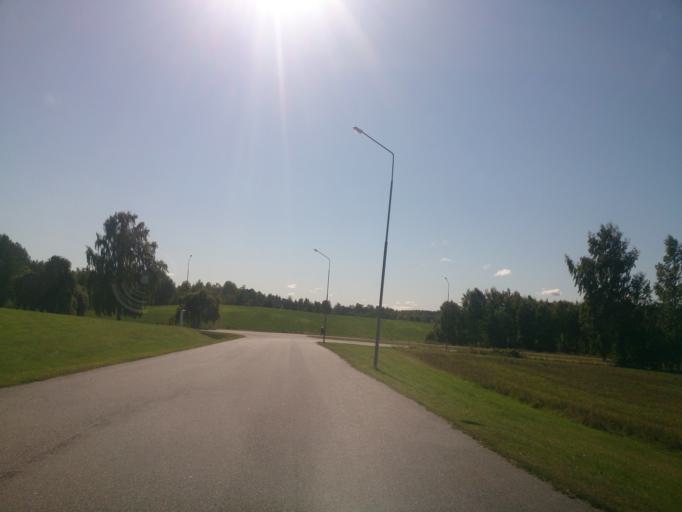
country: SE
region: OEstergoetland
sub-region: Atvidabergs Kommun
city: Atvidaberg
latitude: 58.2267
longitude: 15.9711
